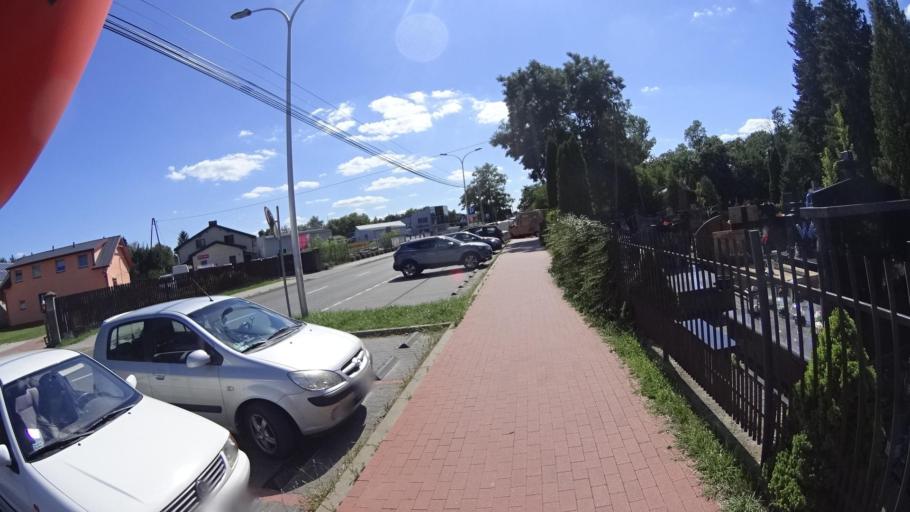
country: PL
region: Masovian Voivodeship
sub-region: Powiat piaseczynski
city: Piaseczno
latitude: 52.0813
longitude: 21.0408
